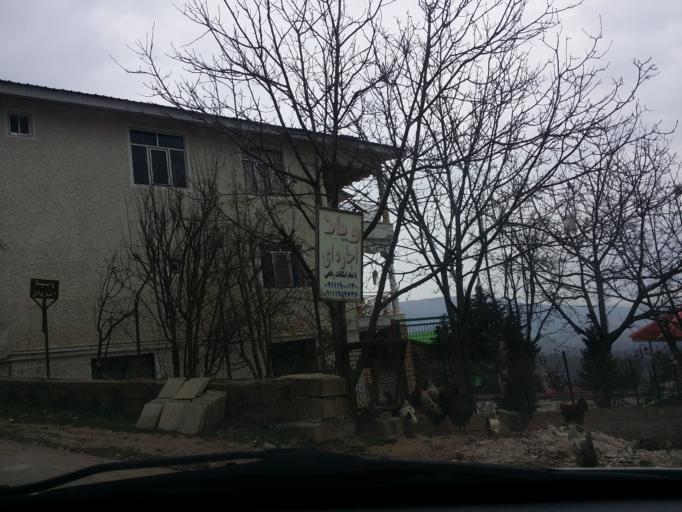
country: IR
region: Mazandaran
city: `Abbasabad
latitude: 36.5325
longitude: 51.1611
